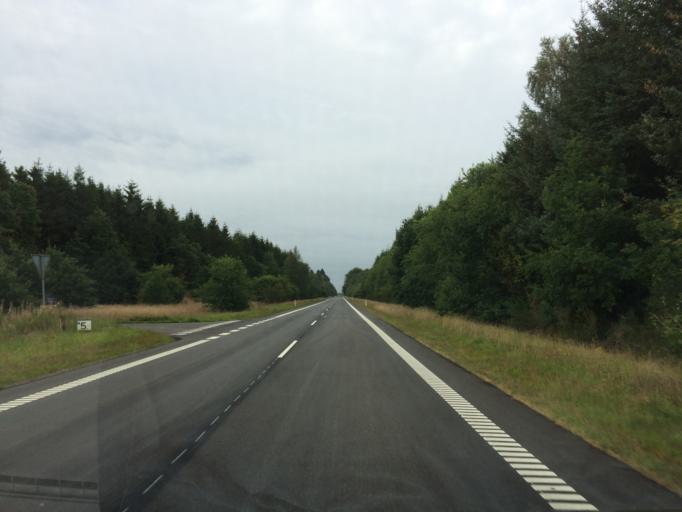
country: DK
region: Central Jutland
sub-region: Herning Kommune
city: Lind
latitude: 56.0566
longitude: 8.9953
